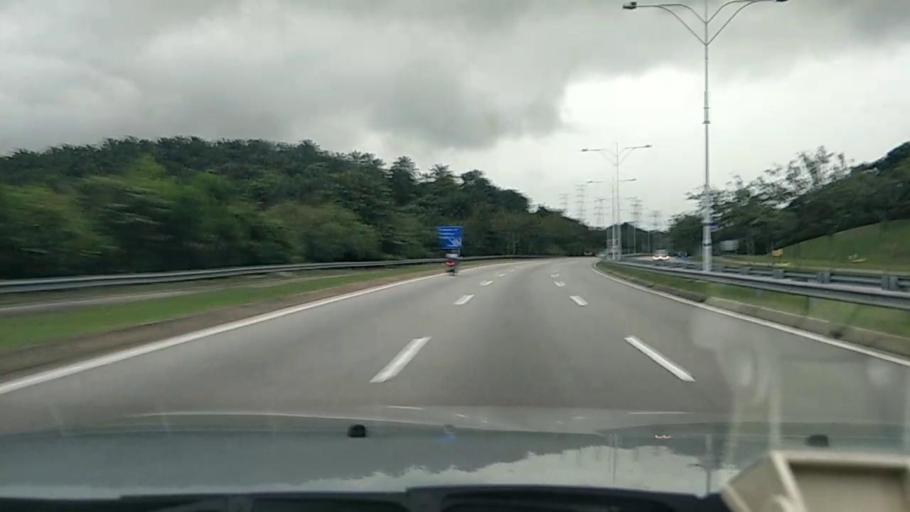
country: MY
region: Putrajaya
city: Putrajaya
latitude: 2.9493
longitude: 101.7132
